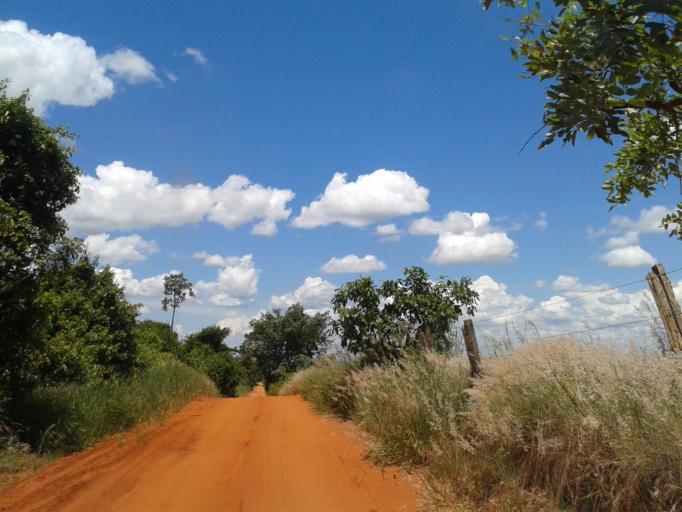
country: BR
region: Minas Gerais
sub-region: Centralina
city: Centralina
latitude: -18.6983
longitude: -49.1558
